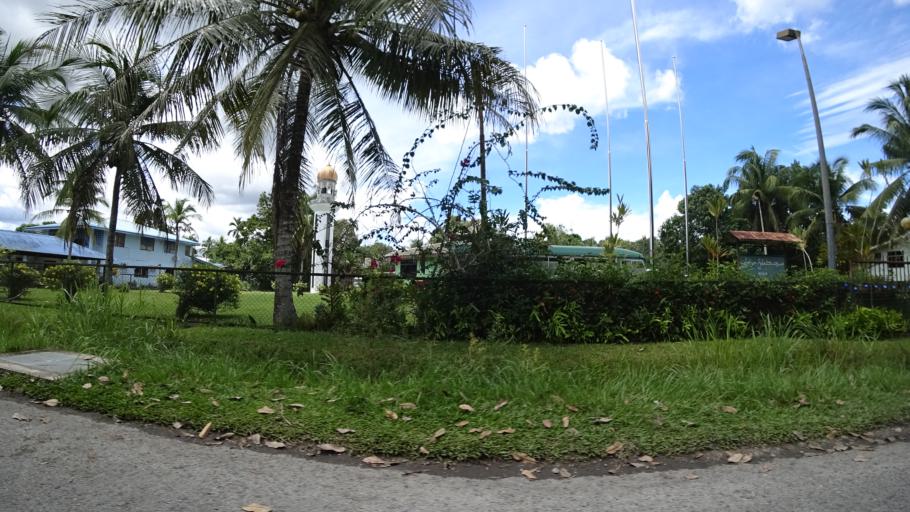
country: MY
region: Sarawak
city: Limbang
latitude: 4.8105
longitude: 114.8540
